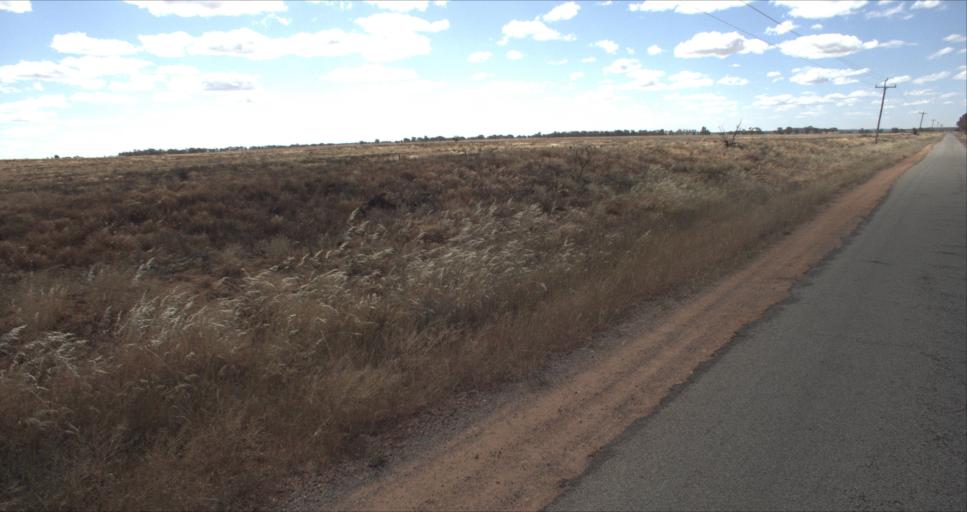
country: AU
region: New South Wales
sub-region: Leeton
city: Leeton
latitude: -34.4797
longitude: 146.2493
